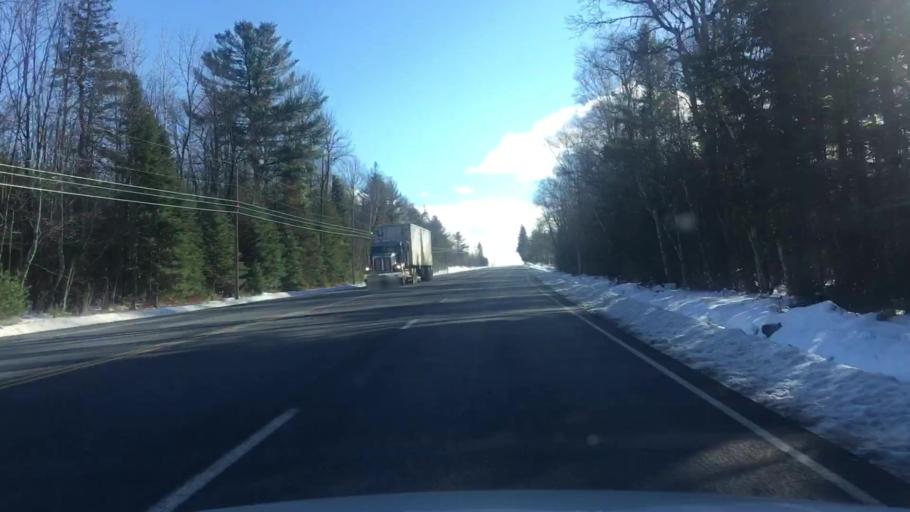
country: US
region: Maine
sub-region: Somerset County
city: Madison
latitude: 44.8979
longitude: -69.8100
